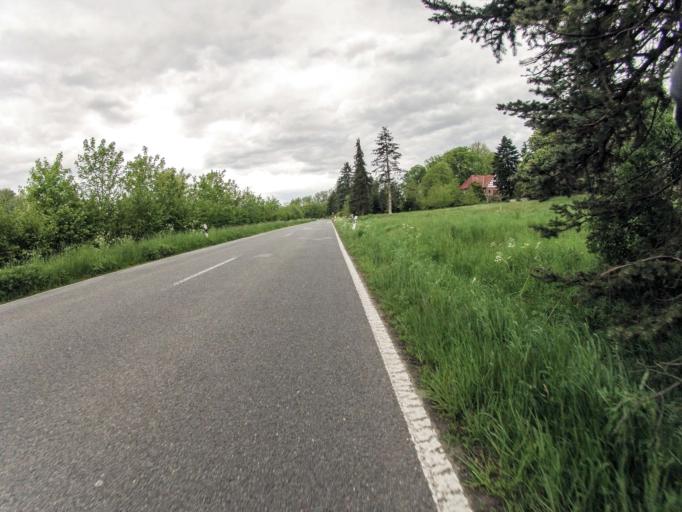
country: DE
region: Lower Saxony
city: Belm
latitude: 52.3397
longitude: 8.1662
